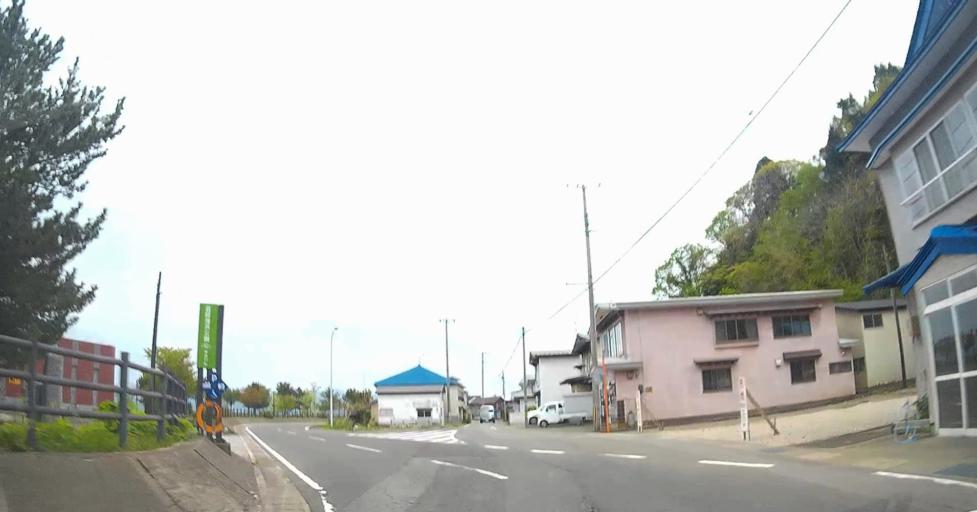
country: JP
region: Aomori
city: Shimokizukuri
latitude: 41.2031
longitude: 140.4280
